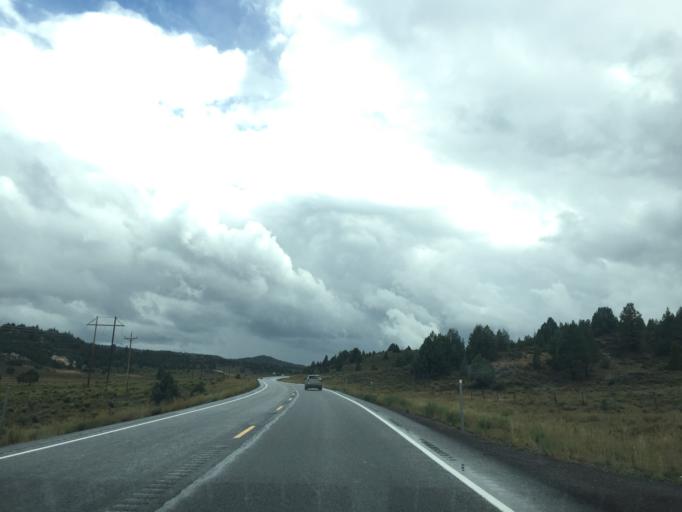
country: US
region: Utah
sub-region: Garfield County
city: Panguitch
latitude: 37.5145
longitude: -112.4978
